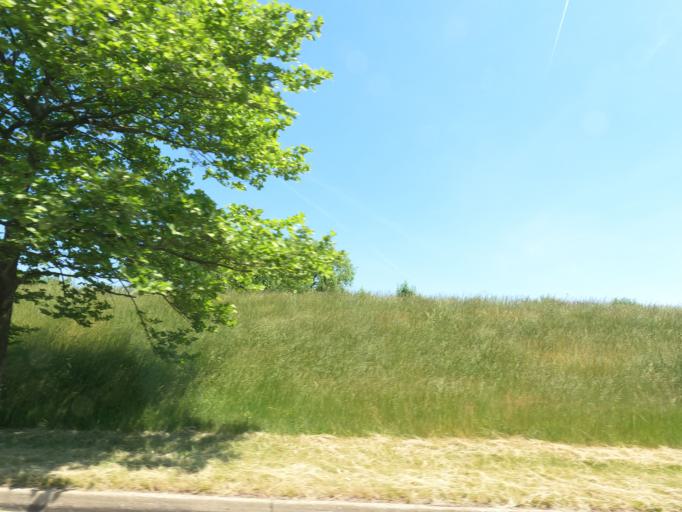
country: US
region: Maryland
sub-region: Howard County
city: Savage
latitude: 39.1764
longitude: -76.8190
